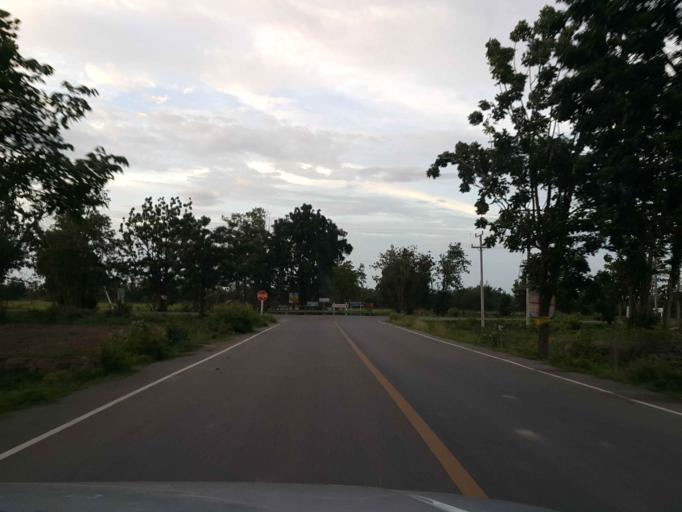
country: TH
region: Sukhothai
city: Ban Dan Lan Hoi
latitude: 17.1035
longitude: 99.5903
